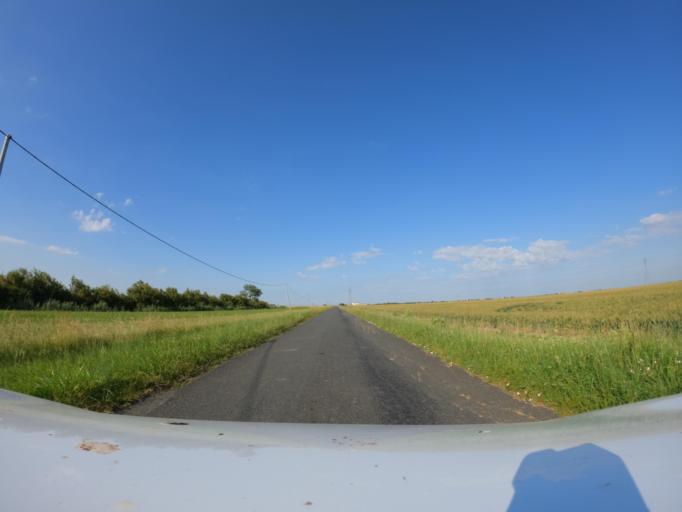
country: FR
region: Poitou-Charentes
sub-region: Departement de la Charente-Maritime
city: Charron
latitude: 46.3366
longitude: -1.0943
